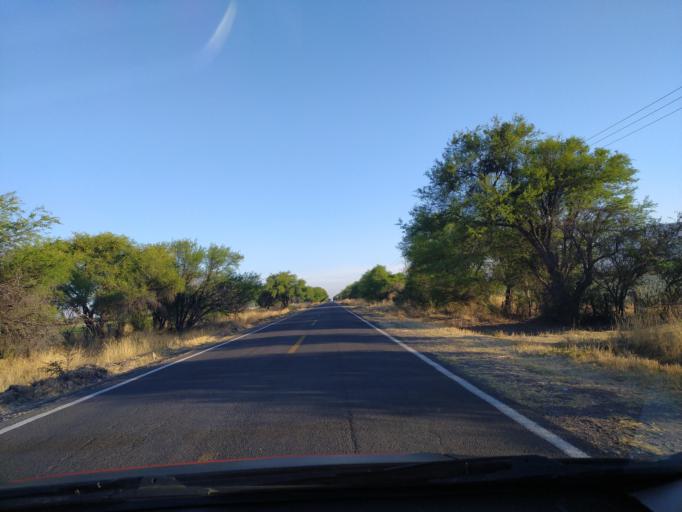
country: MX
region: Guanajuato
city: Ciudad Manuel Doblado
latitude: 20.7574
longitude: -101.8269
